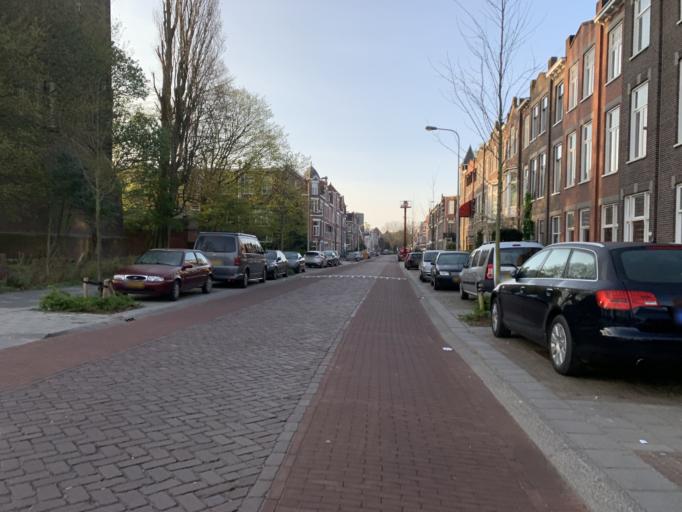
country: NL
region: Groningen
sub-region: Gemeente Groningen
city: Groningen
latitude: 53.2189
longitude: 6.5487
